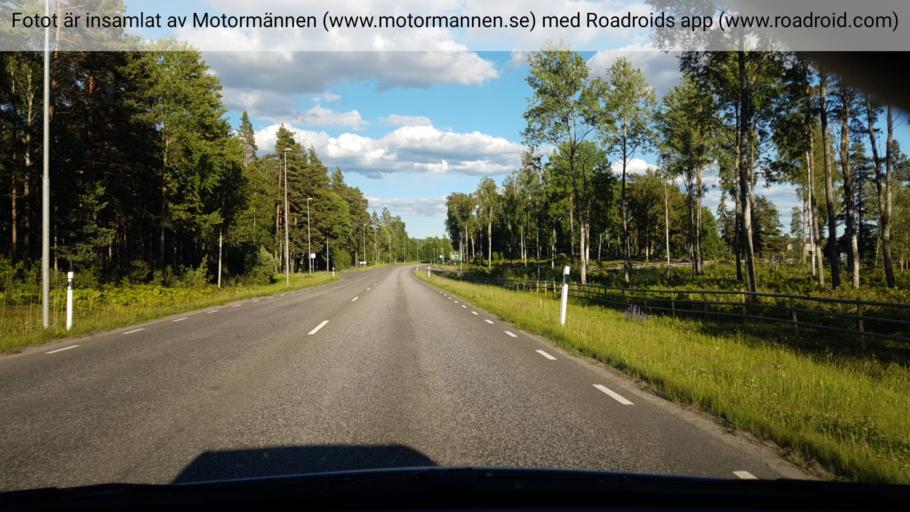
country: SE
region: Vaestra Goetaland
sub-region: Tidaholms Kommun
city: Tidaholm
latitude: 58.1922
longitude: 13.9377
